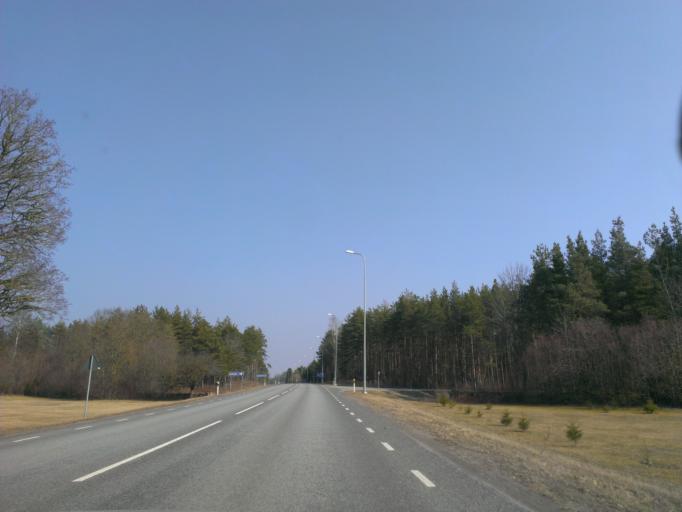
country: EE
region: Saare
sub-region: Orissaare vald
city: Orissaare
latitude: 58.5189
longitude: 22.8916
